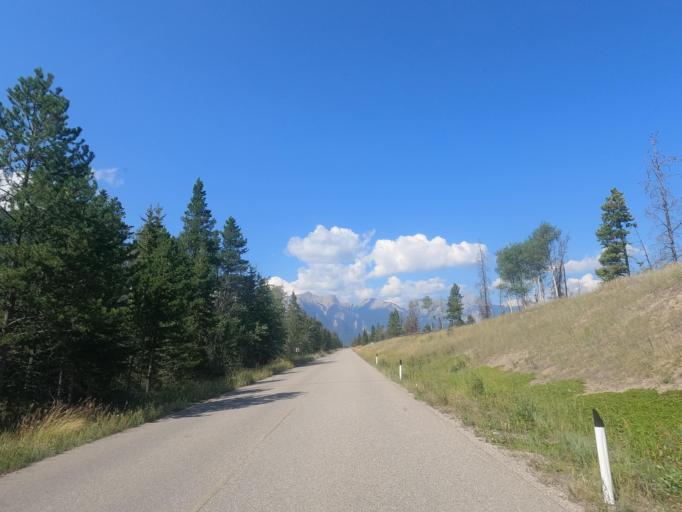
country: CA
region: Alberta
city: Jasper Park Lodge
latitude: 52.9732
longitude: -118.0615
